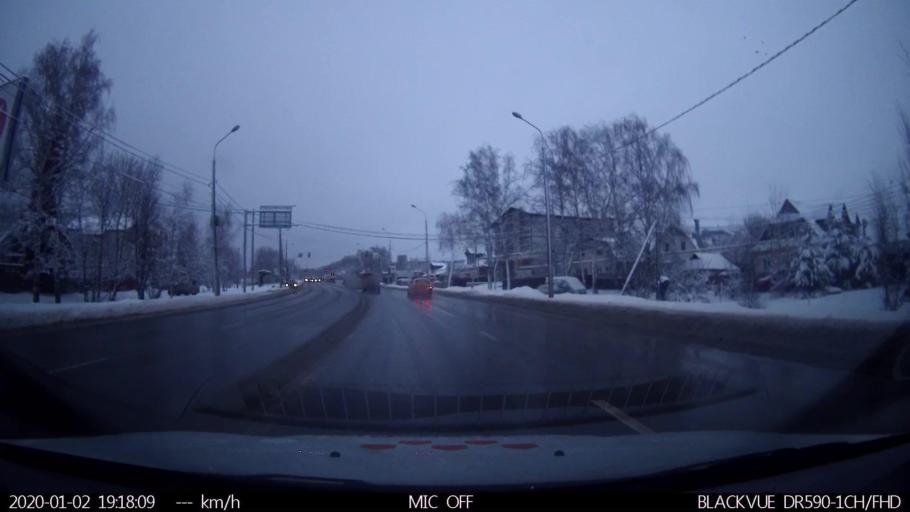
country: RU
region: Nizjnij Novgorod
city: Nizhniy Novgorod
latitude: 56.2174
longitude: 43.9320
